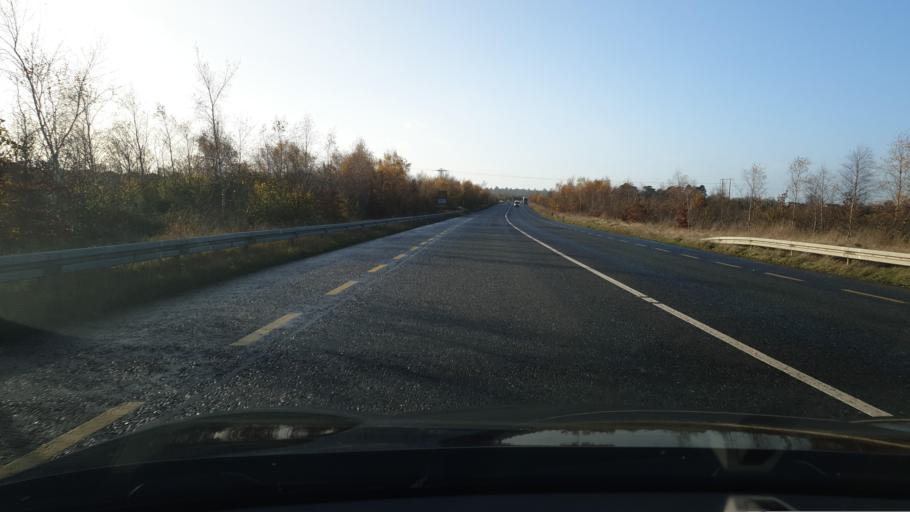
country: IE
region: Leinster
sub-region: An Mhi
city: Dunboyne
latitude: 53.4286
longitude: -6.4813
